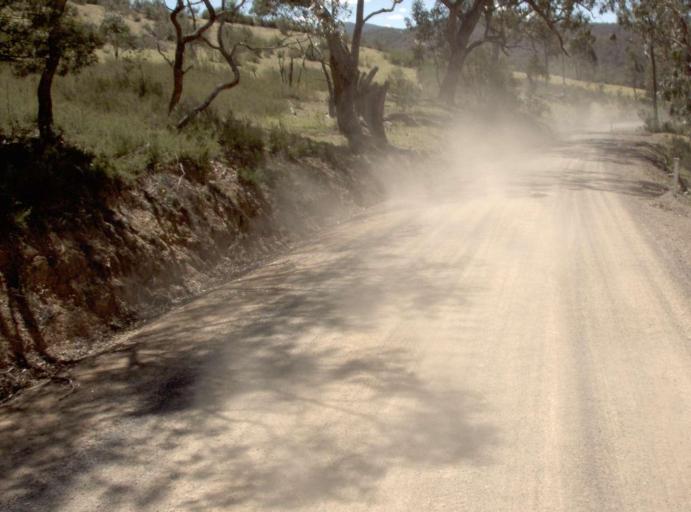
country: AU
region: New South Wales
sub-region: Snowy River
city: Jindabyne
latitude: -37.0440
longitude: 148.5601
